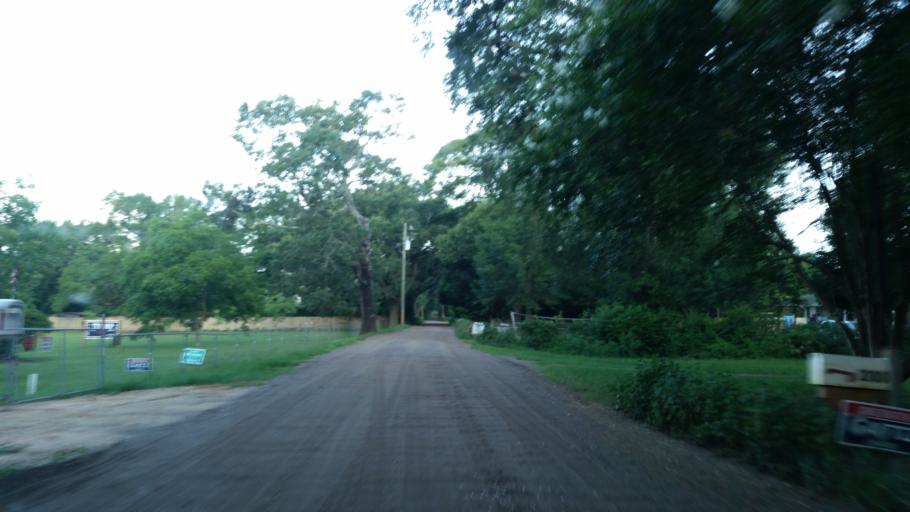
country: US
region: Florida
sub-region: Escambia County
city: Ensley
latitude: 30.5273
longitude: -87.3072
